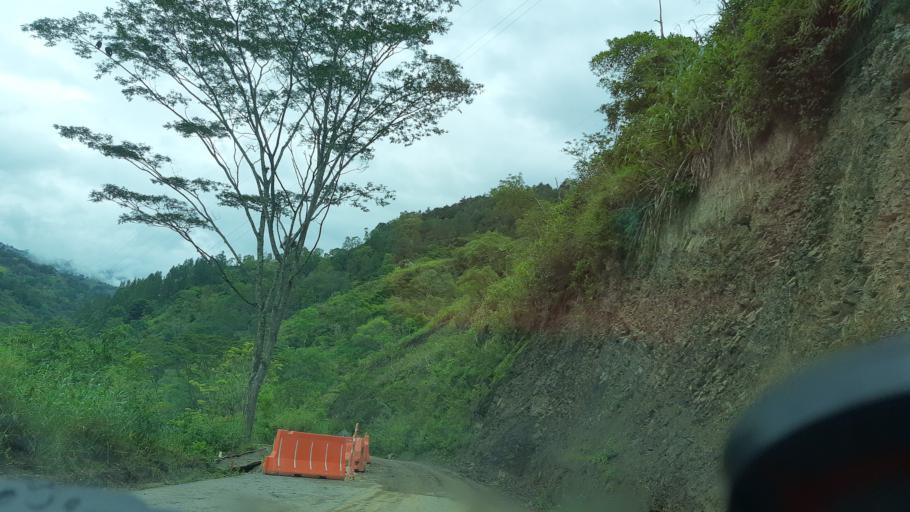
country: CO
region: Cundinamarca
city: Tenza
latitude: 5.0749
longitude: -73.3997
